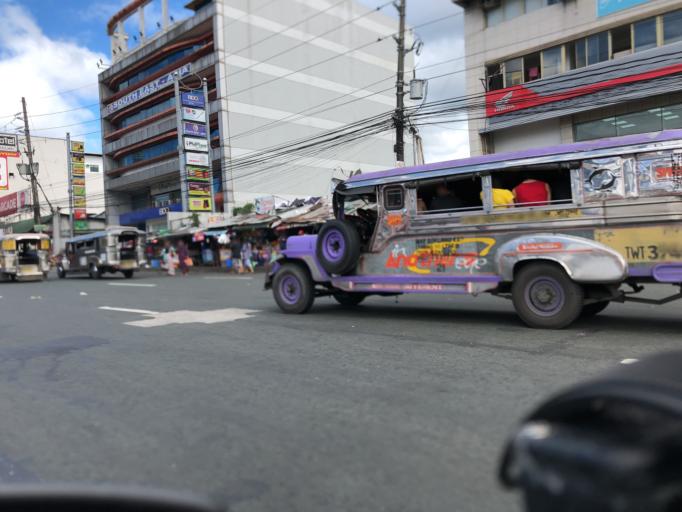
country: PH
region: Calabarzon
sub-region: Province of Rizal
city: San Mateo
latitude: 14.7330
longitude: 121.0612
